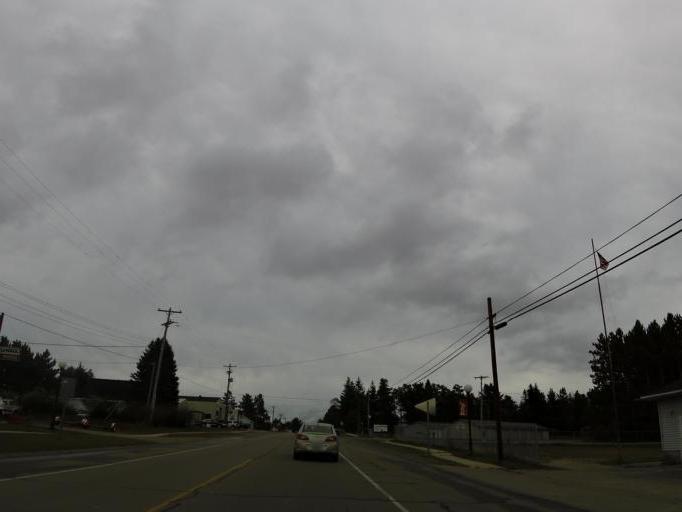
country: US
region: Michigan
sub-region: Roscommon County
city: Roscommon
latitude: 44.4951
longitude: -84.5867
